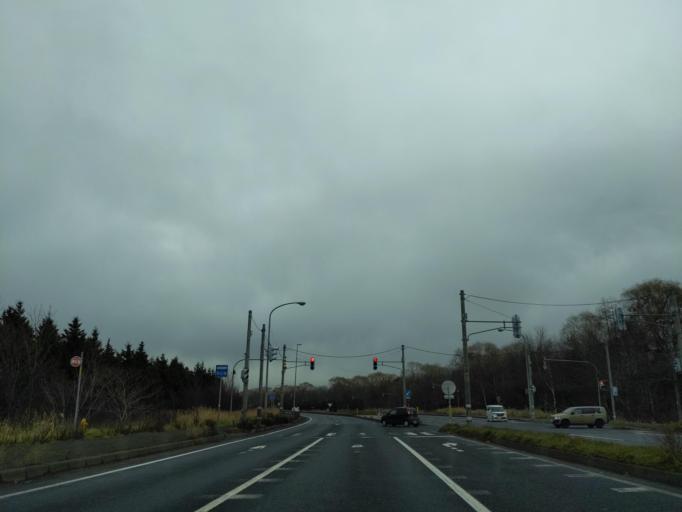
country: JP
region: Hokkaido
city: Ishikari
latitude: 43.1686
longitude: 141.4013
